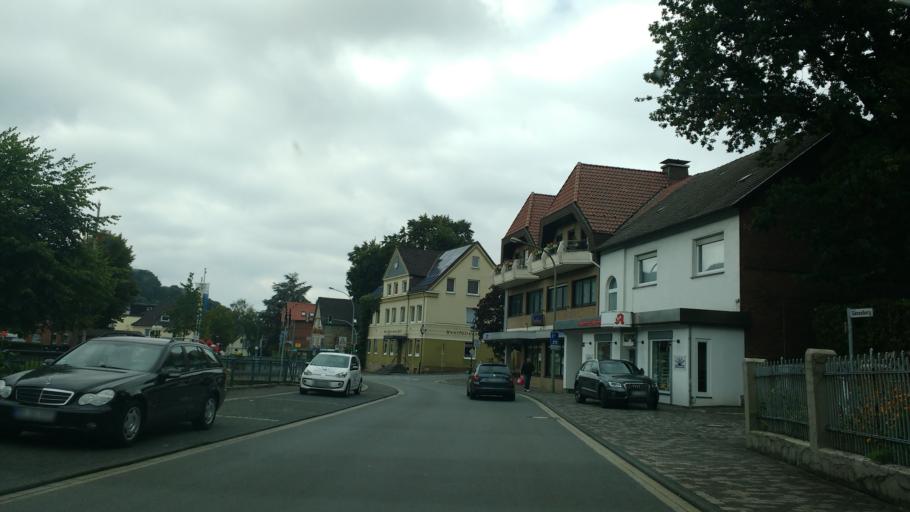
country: DE
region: North Rhine-Westphalia
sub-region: Regierungsbezirk Detmold
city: Altenbeken
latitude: 51.7637
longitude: 8.9429
